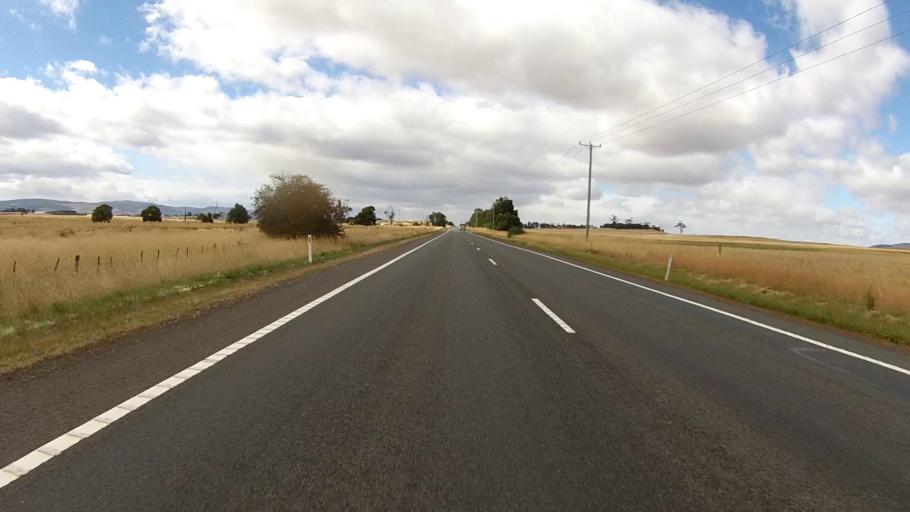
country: AU
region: Tasmania
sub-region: Northern Midlands
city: Evandale
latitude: -41.8984
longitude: 147.4748
